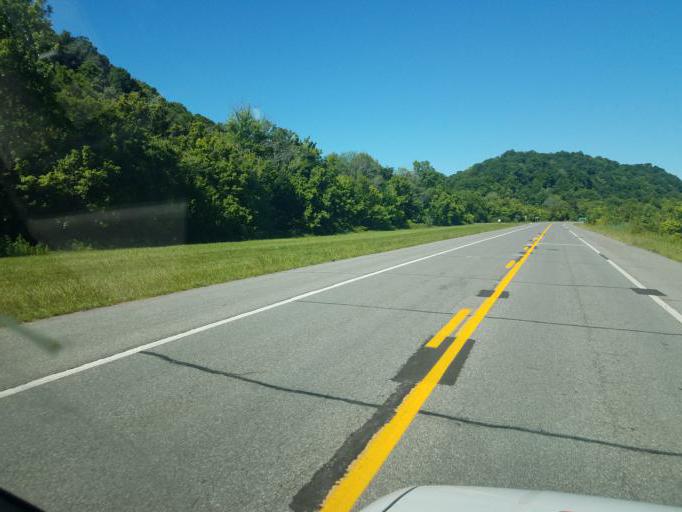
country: US
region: West Virginia
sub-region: Cabell County
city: Lesage
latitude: 38.5844
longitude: -82.2250
